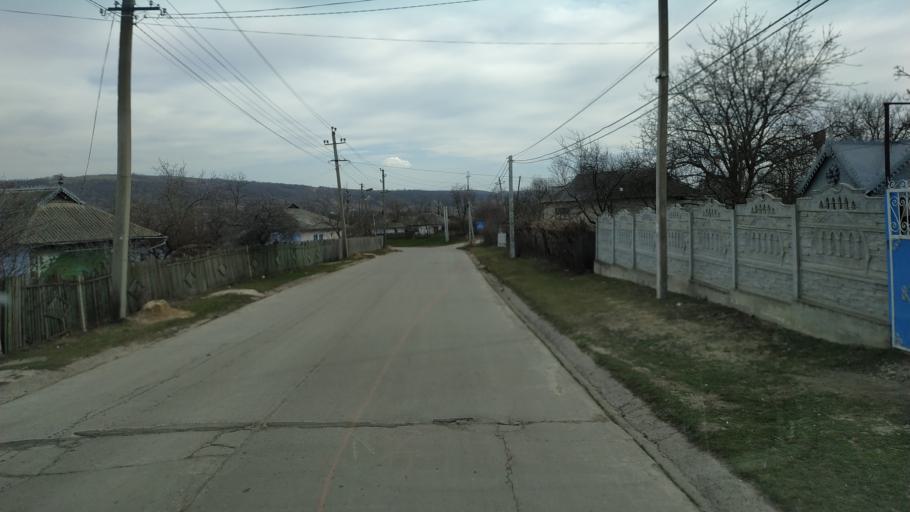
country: MD
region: Nisporeni
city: Nisporeni
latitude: 46.9270
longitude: 28.2615
